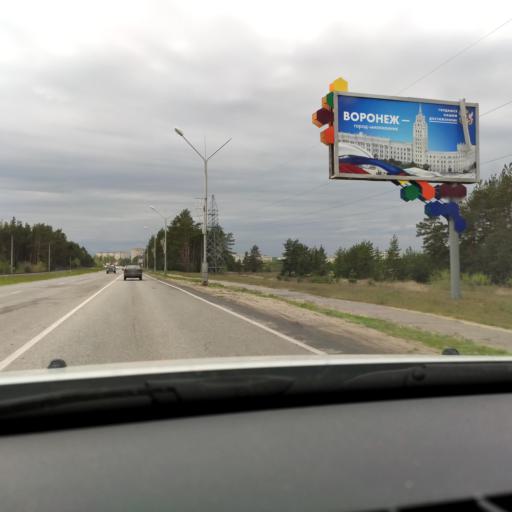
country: RU
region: Voronezj
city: Novovoronezh
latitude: 51.3239
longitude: 39.2355
